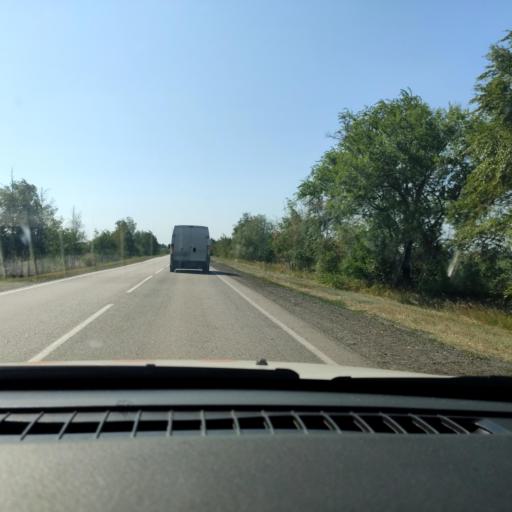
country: RU
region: Voronezj
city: Ostrogozhsk
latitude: 50.8021
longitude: 39.3244
